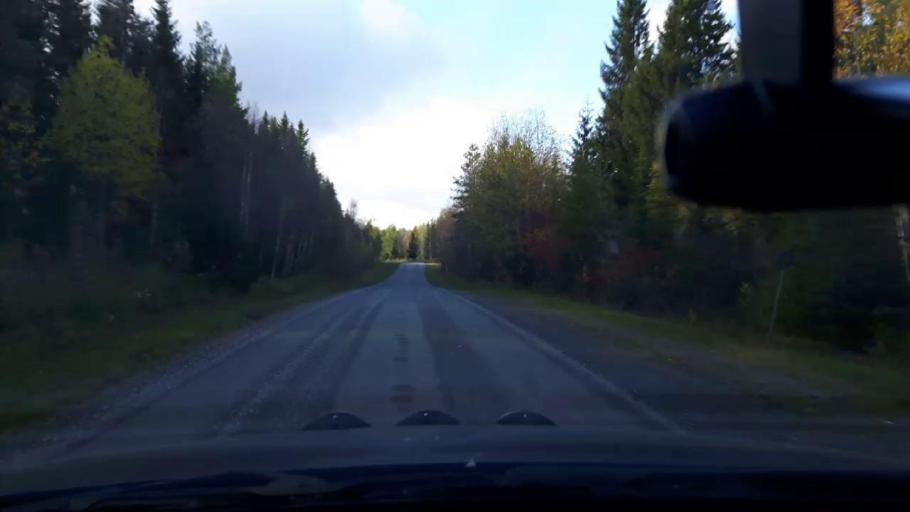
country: SE
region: Jaemtland
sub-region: Bergs Kommun
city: Hoverberg
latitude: 63.0260
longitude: 14.2846
